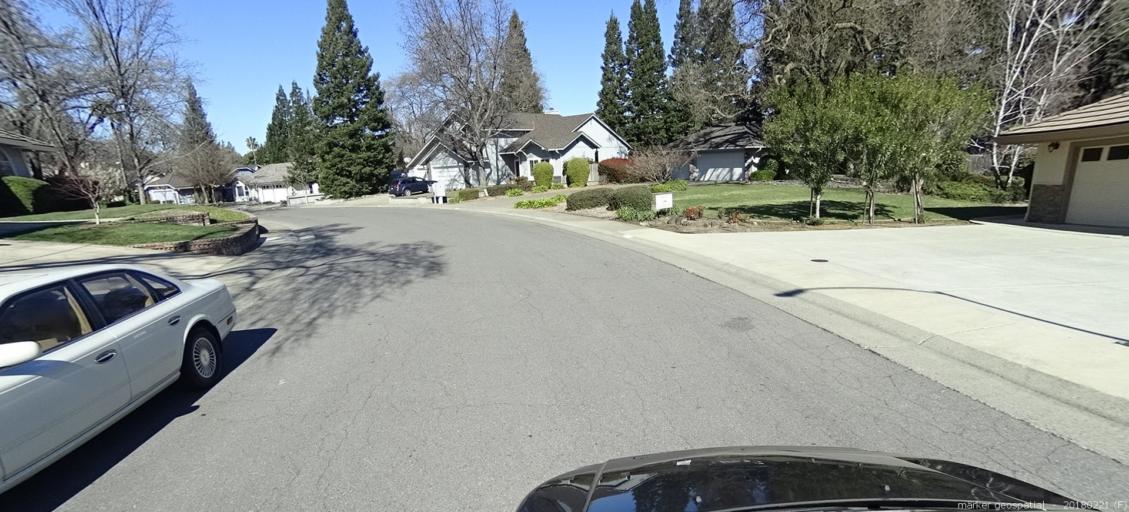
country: US
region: California
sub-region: Sacramento County
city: Orangevale
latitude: 38.6957
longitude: -121.2426
